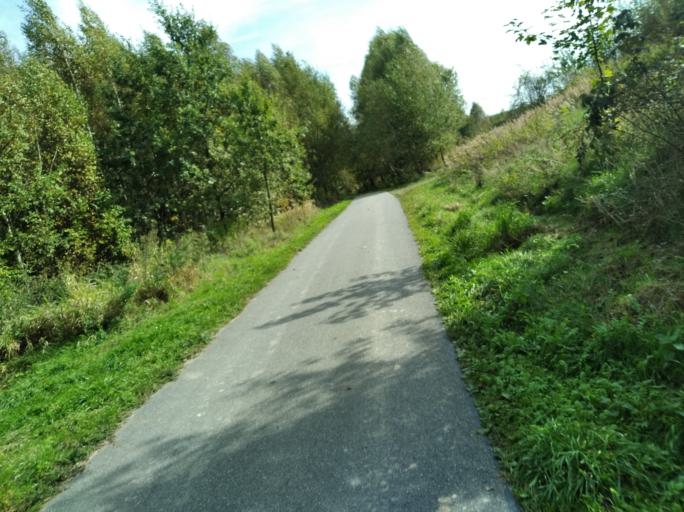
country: PL
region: Subcarpathian Voivodeship
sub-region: Powiat strzyzowski
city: Jawornik
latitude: 49.8379
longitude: 21.8834
